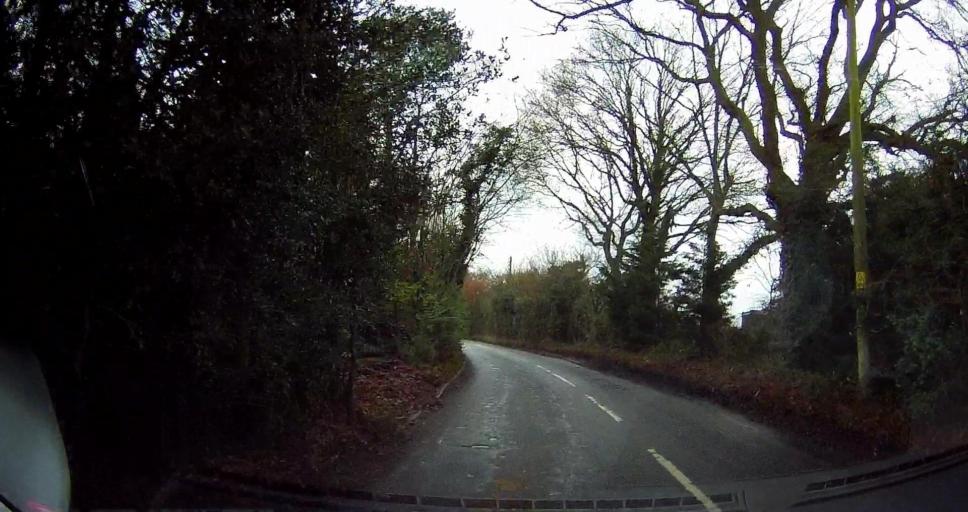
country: GB
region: England
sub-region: Kent
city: Biggin Hill
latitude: 51.3247
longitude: 0.0718
